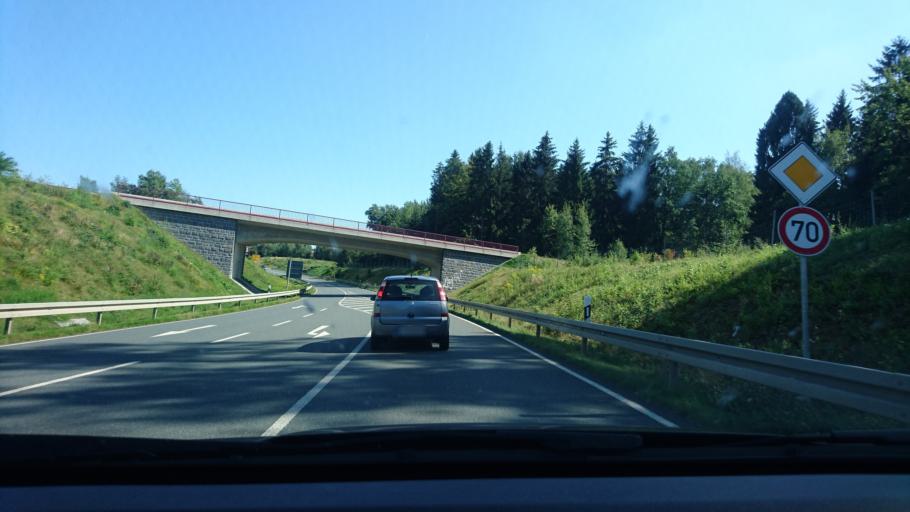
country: DE
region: Saxony
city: Lengenfeld
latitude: 50.5417
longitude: 12.3447
